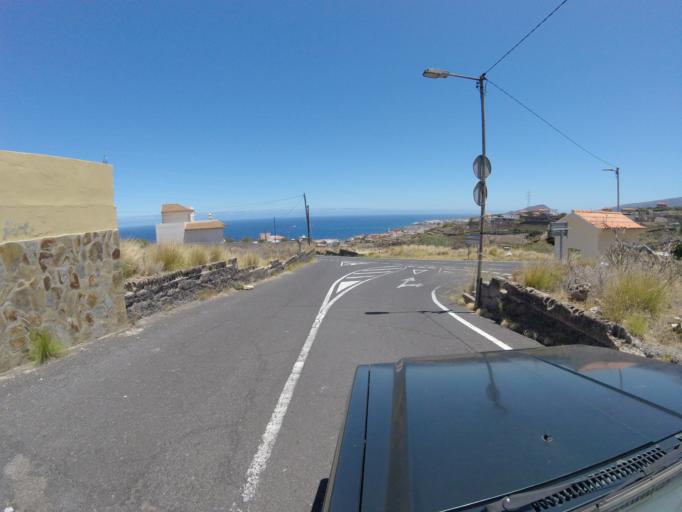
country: ES
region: Canary Islands
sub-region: Provincia de Santa Cruz de Tenerife
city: Candelaria
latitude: 28.3644
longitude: -16.3777
